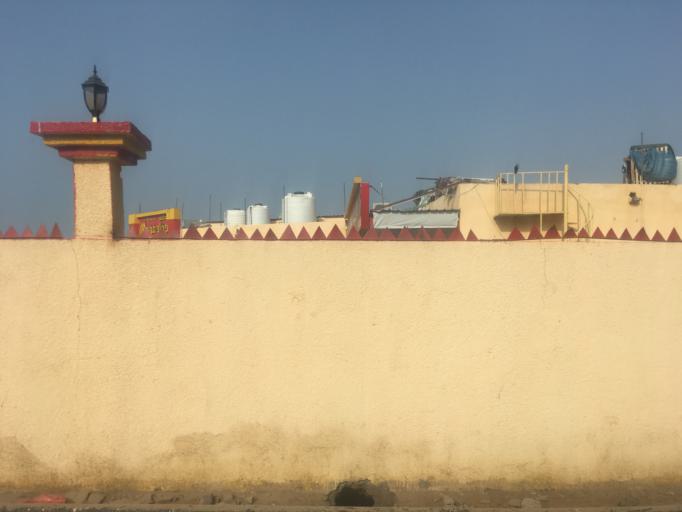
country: YE
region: Aden
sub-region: Attawahi
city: At Tawahi
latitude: 12.7753
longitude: 44.9868
